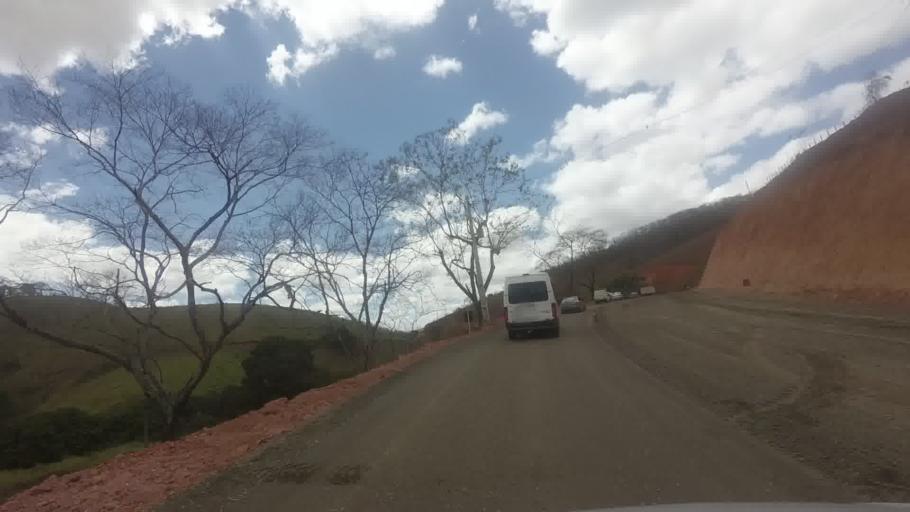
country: BR
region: Rio de Janeiro
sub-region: Santo Antonio De Padua
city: Santo Antonio de Padua
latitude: -21.5107
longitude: -42.0909
